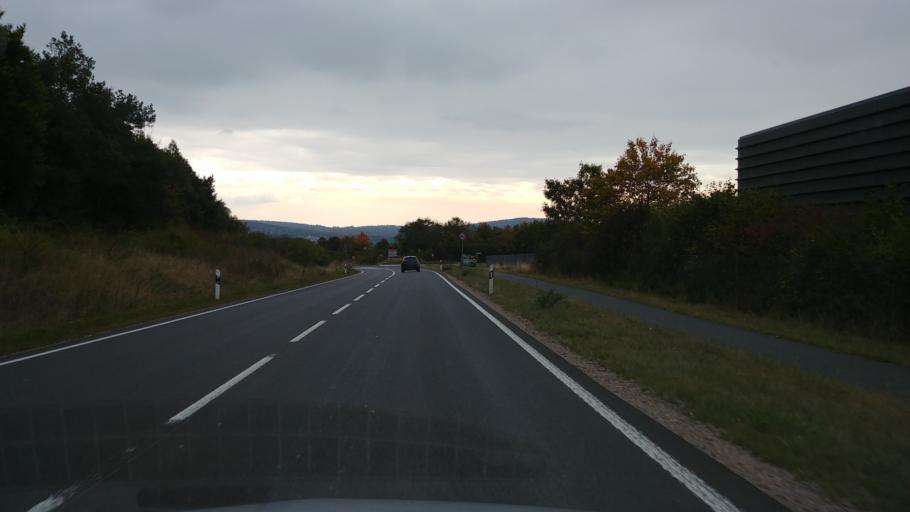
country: DE
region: Hesse
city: Taunusstein
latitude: 50.1832
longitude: 8.2032
